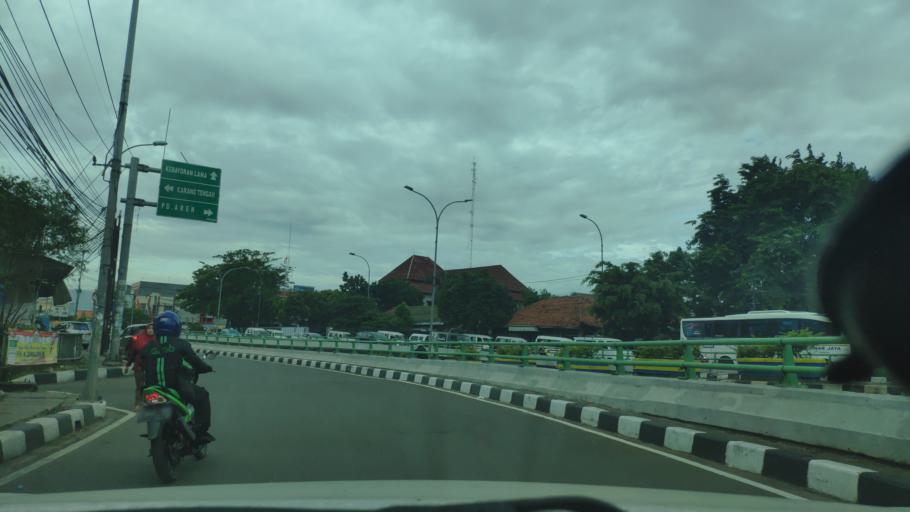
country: ID
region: West Java
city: Ciputat
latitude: -6.2252
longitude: 106.7038
